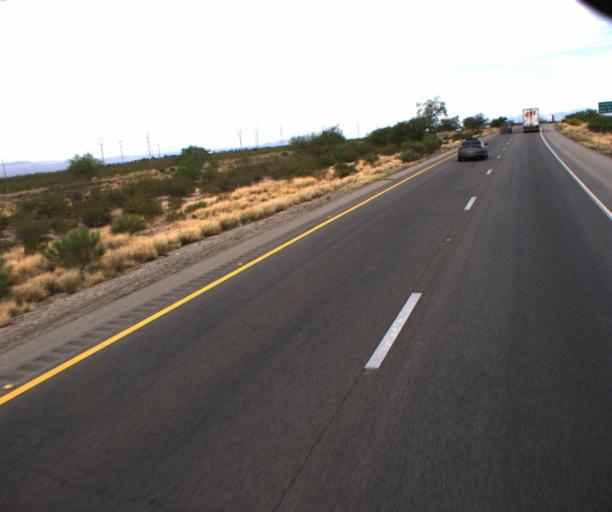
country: US
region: Arizona
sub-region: Pima County
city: Vail
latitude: 32.0463
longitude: -110.7485
